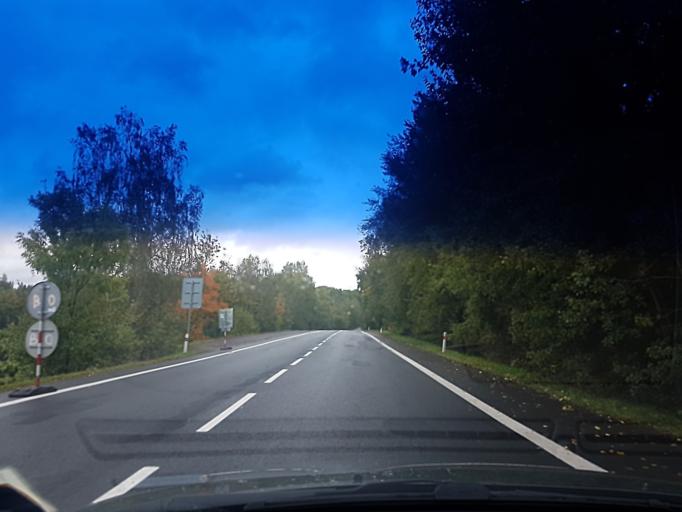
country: CZ
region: Karlovarsky
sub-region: Okres Cheb
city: Cheb
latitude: 50.0810
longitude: 12.3326
